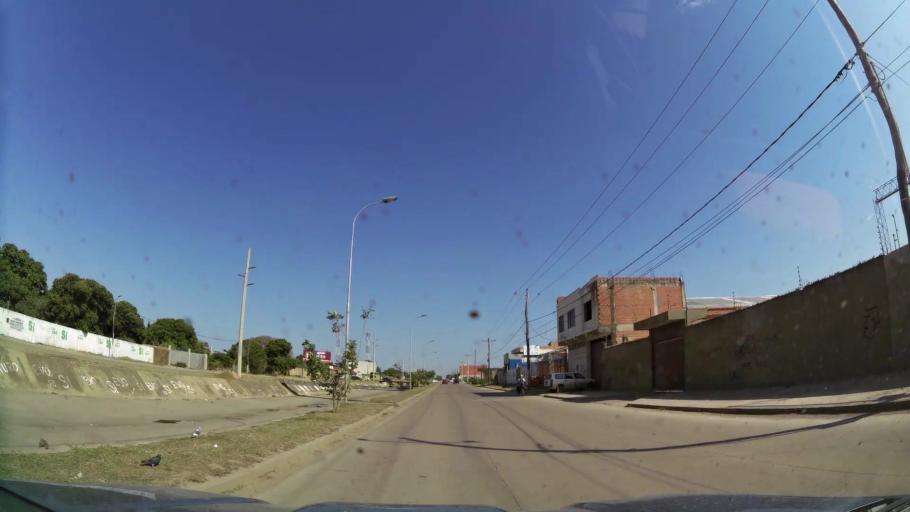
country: BO
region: Santa Cruz
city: Cotoca
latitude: -17.7912
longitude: -63.1085
